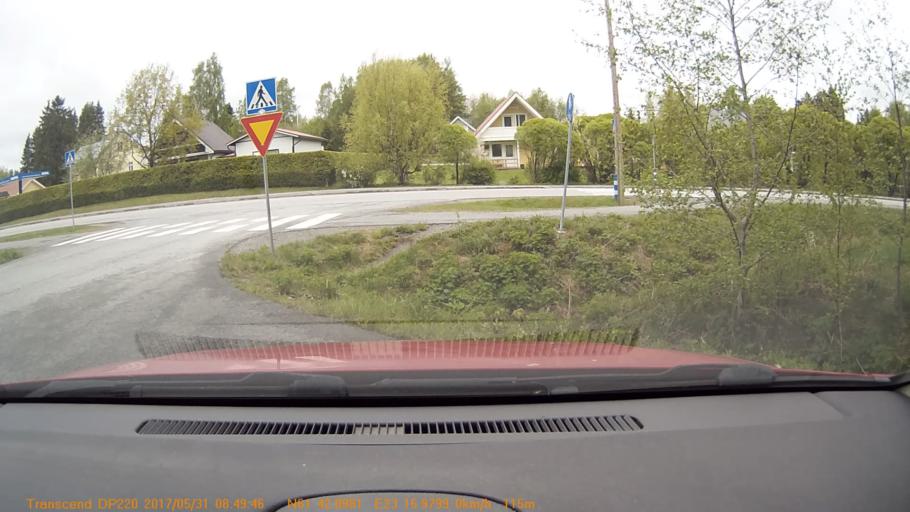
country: FI
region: Pirkanmaa
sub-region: Tampere
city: Viljakkala
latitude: 61.7016
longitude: 23.2662
